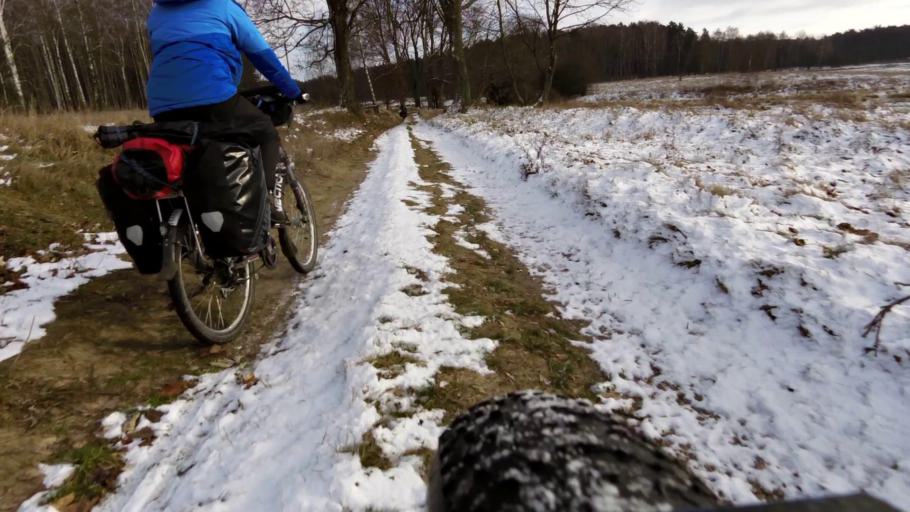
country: PL
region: West Pomeranian Voivodeship
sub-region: Powiat walecki
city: Tuczno
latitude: 53.3005
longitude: 16.2826
